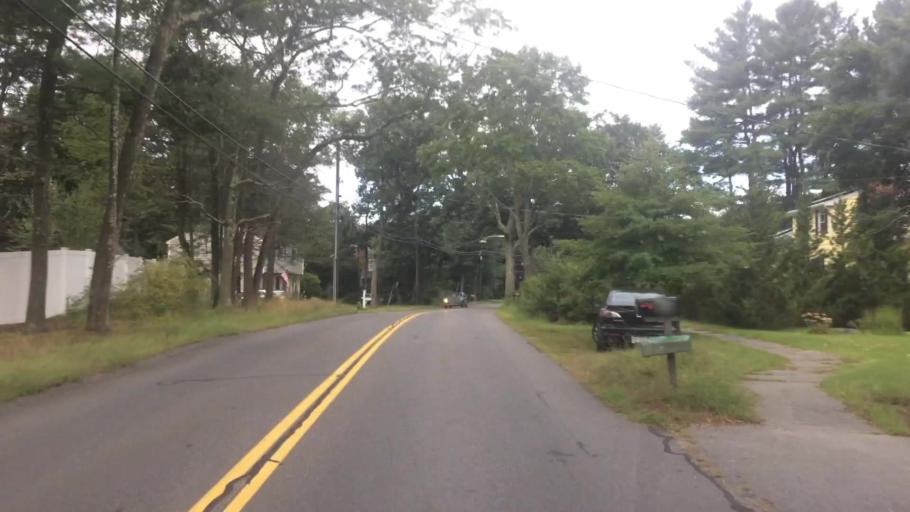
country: US
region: Massachusetts
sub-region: Middlesex County
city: West Concord
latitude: 42.4588
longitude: -71.4100
